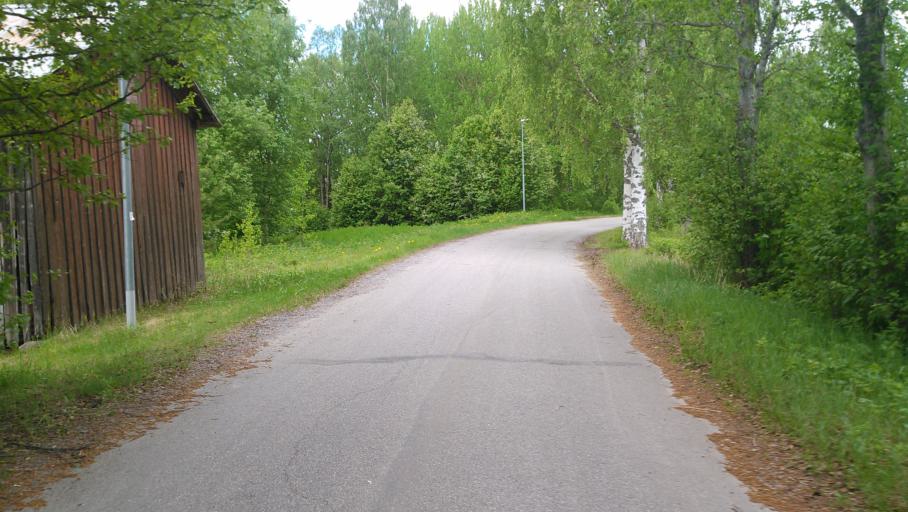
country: SE
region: Vaesterbotten
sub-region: Umea Kommun
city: Roback
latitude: 63.8586
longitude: 20.0897
